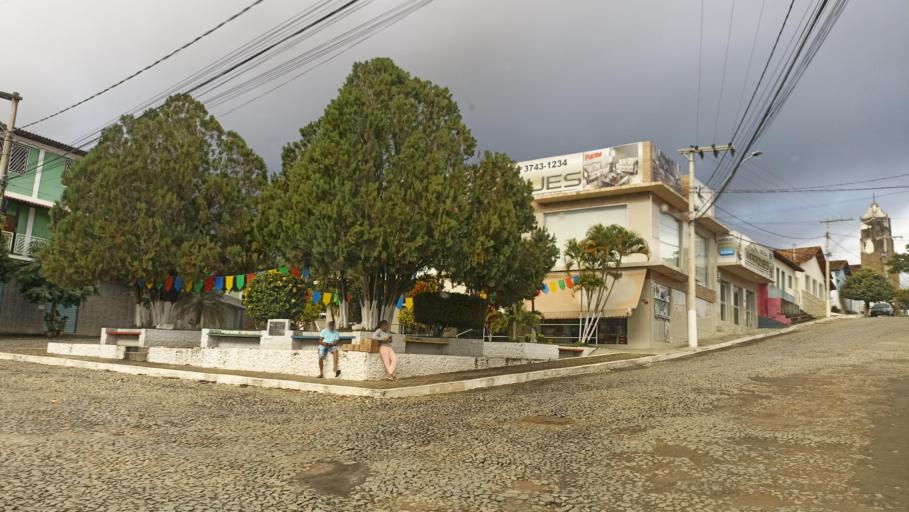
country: BR
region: Minas Gerais
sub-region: Joaima
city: Joaima
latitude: -16.6392
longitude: -40.7626
